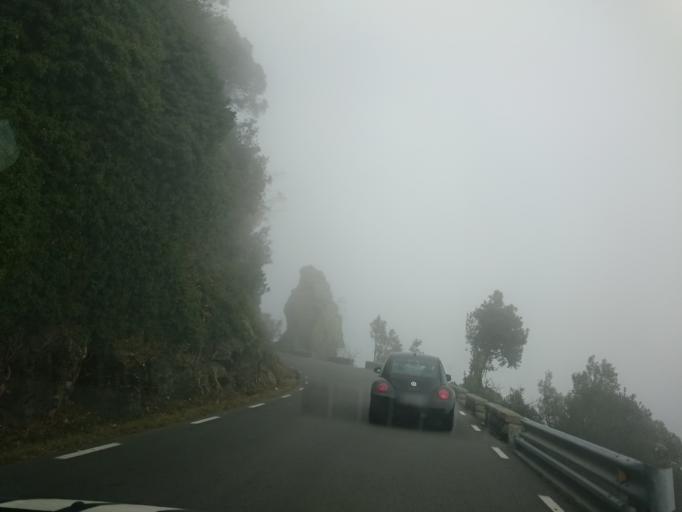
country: ES
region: Catalonia
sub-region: Provincia de Barcelona
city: Fogars de Montclus
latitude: 41.7556
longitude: 2.4723
